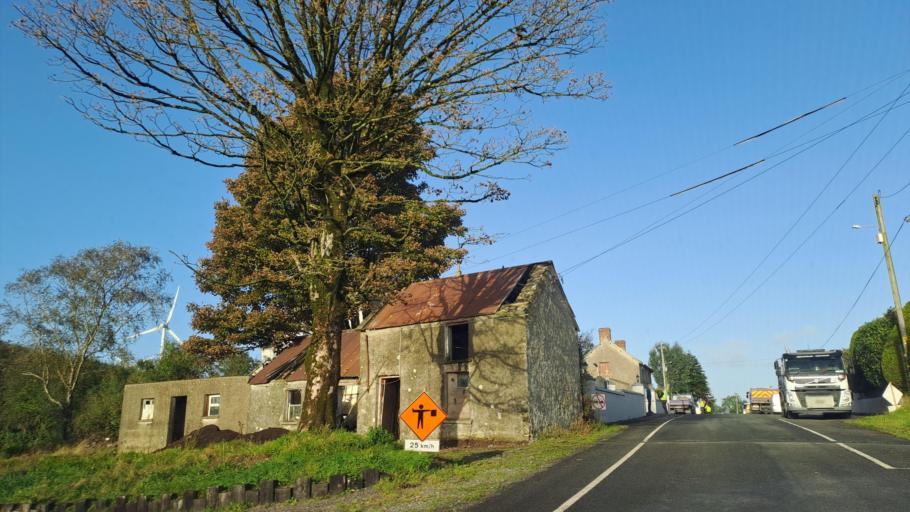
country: IE
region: Ulster
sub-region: County Monaghan
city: Castleblayney
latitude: 54.0853
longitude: -6.8605
